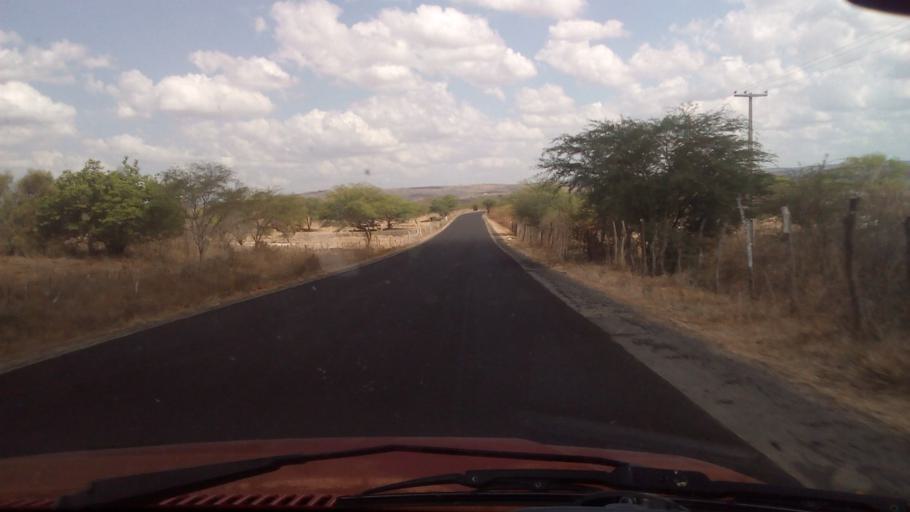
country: BR
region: Paraiba
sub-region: Cacimba De Dentro
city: Cacimba de Dentro
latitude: -6.6682
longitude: -35.7557
